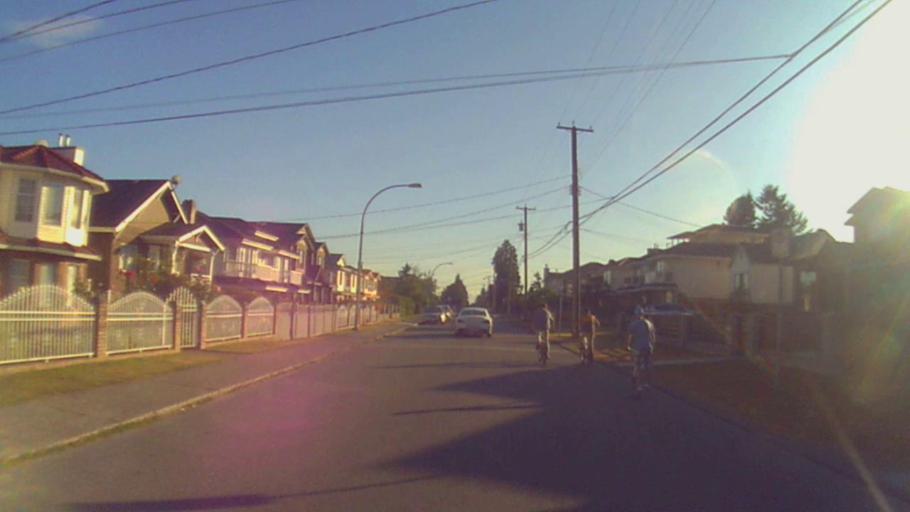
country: CA
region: British Columbia
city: New Westminster
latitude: 49.2255
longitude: -122.9202
